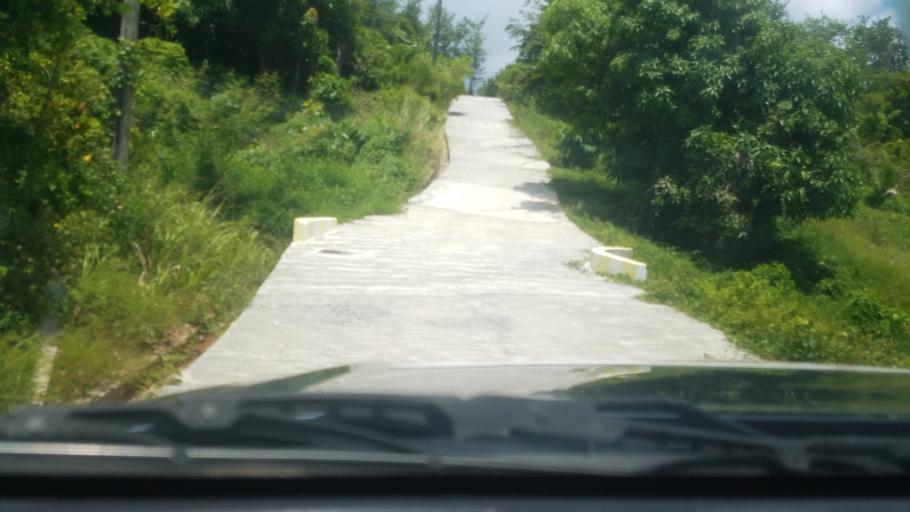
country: LC
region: Dennery Quarter
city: Dennery
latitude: 13.9183
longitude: -60.9023
